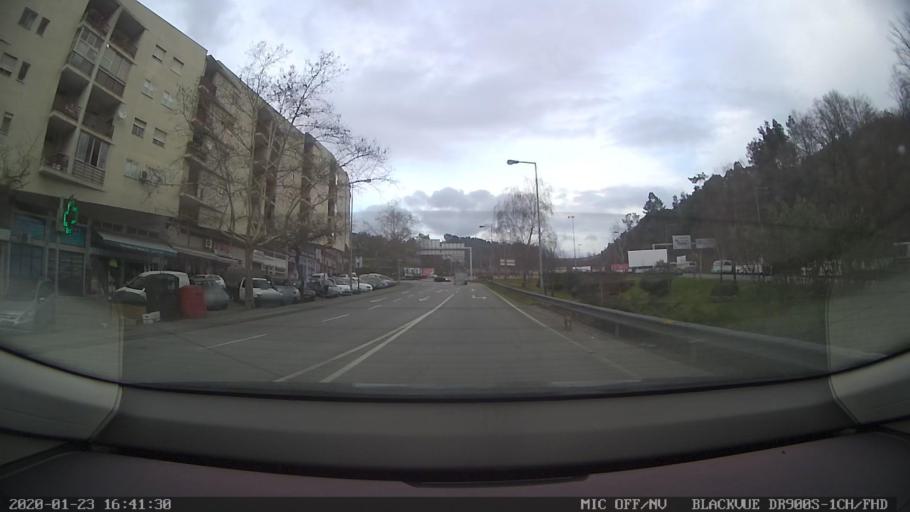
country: PT
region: Porto
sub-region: Amarante
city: Amarante
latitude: 41.2655
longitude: -8.0701
